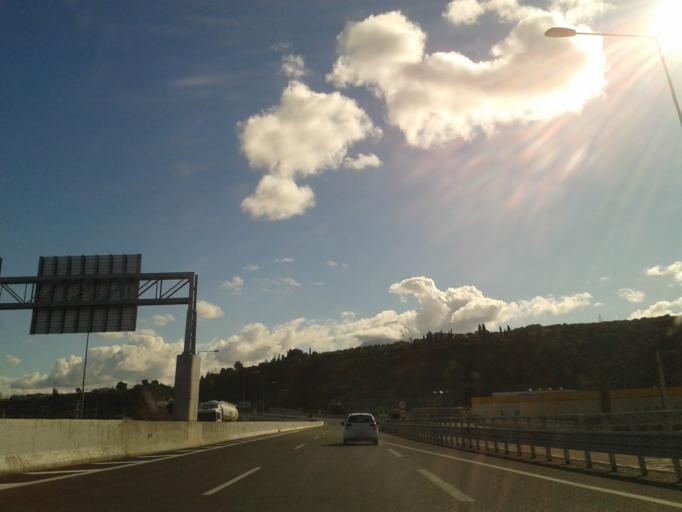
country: GR
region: West Greece
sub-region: Nomos Achaias
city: Aigio
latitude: 38.2607
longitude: 22.0605
